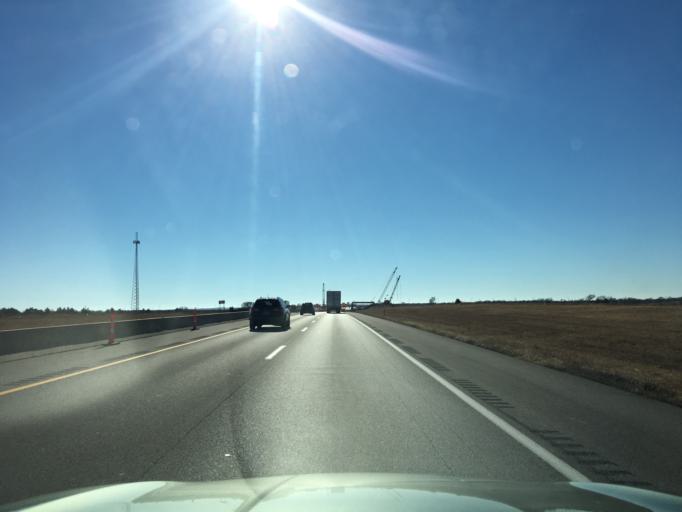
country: US
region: Kansas
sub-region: Sumner County
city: Wellington
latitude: 37.2512
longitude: -97.3390
